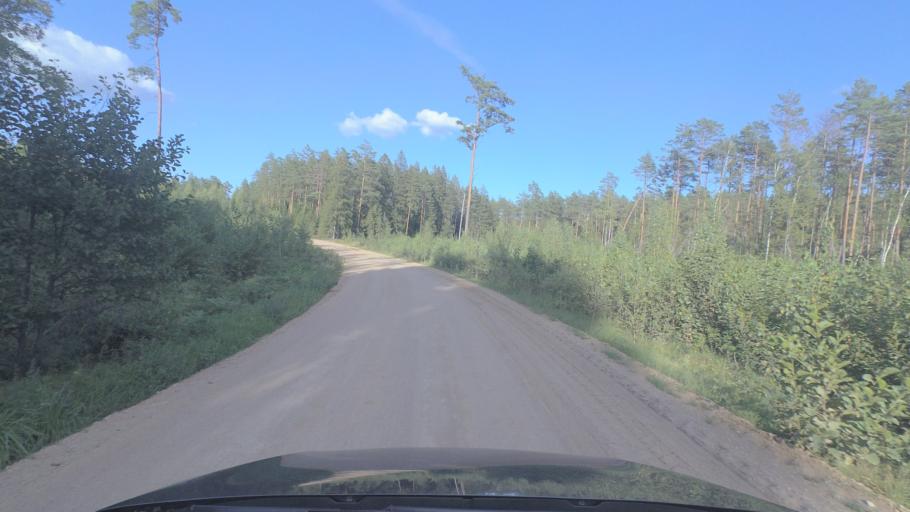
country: LT
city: Pabrade
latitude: 55.1621
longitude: 25.8267
